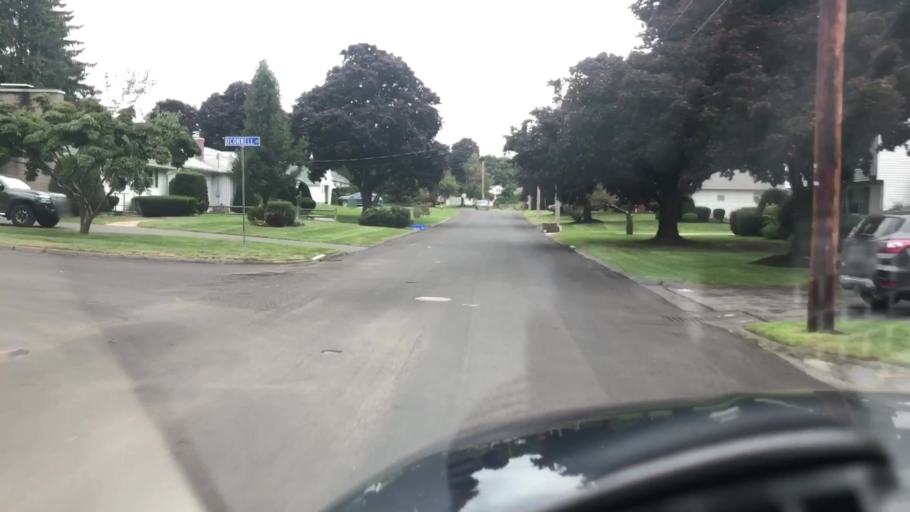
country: US
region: Massachusetts
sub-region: Hampden County
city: Holyoke
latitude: 42.1820
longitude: -72.6499
